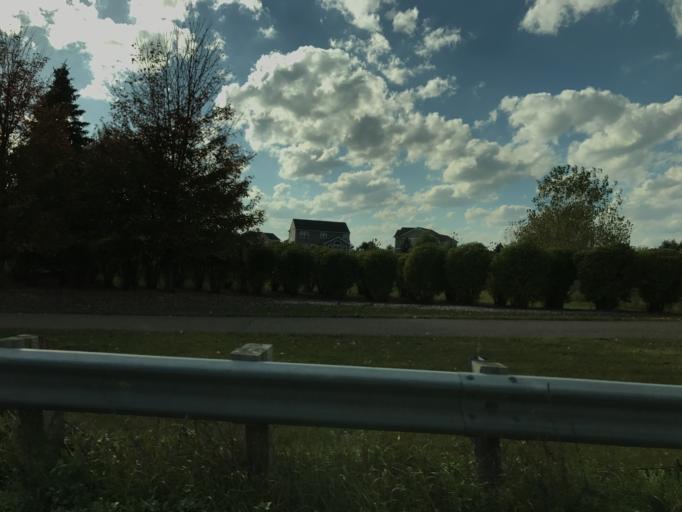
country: US
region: Michigan
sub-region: Oakland County
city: South Lyon
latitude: 42.4774
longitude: -83.6133
